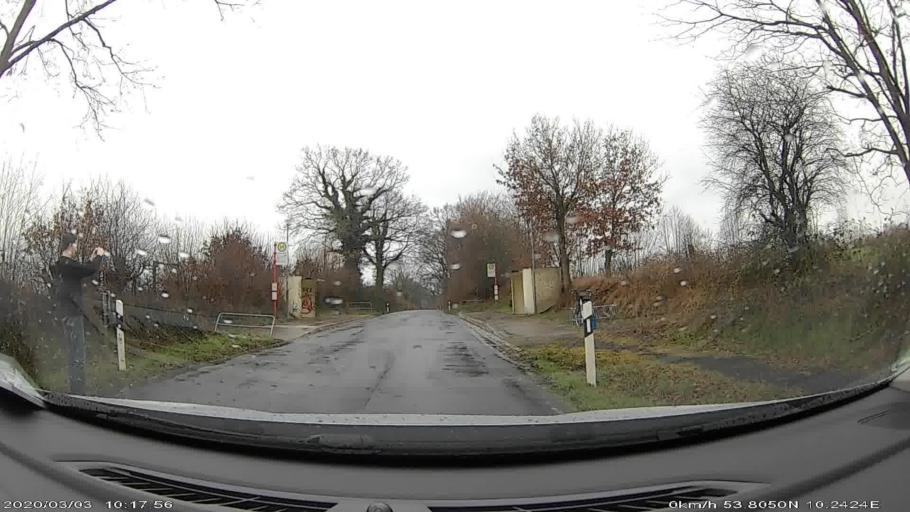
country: DE
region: Schleswig-Holstein
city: Sulfeld
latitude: 53.8043
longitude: 10.2430
